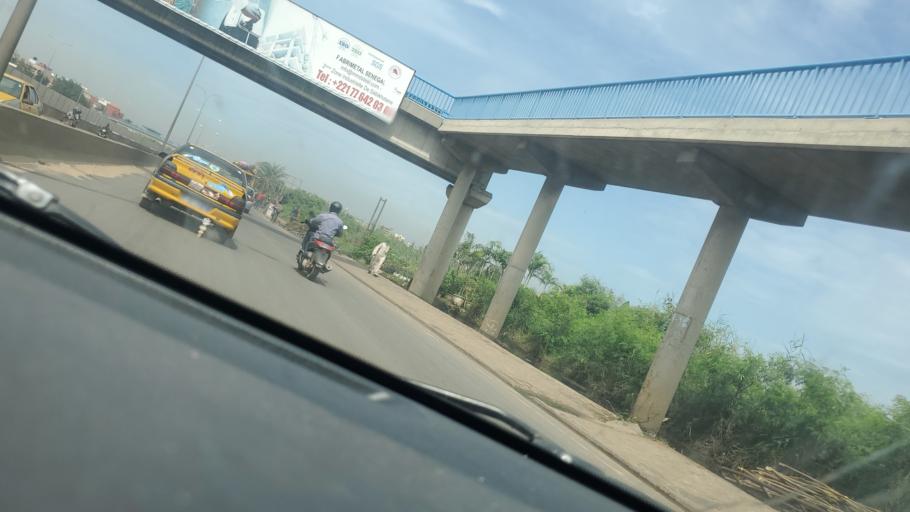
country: SN
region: Dakar
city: Grand Dakar
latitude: 14.7439
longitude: -17.4297
